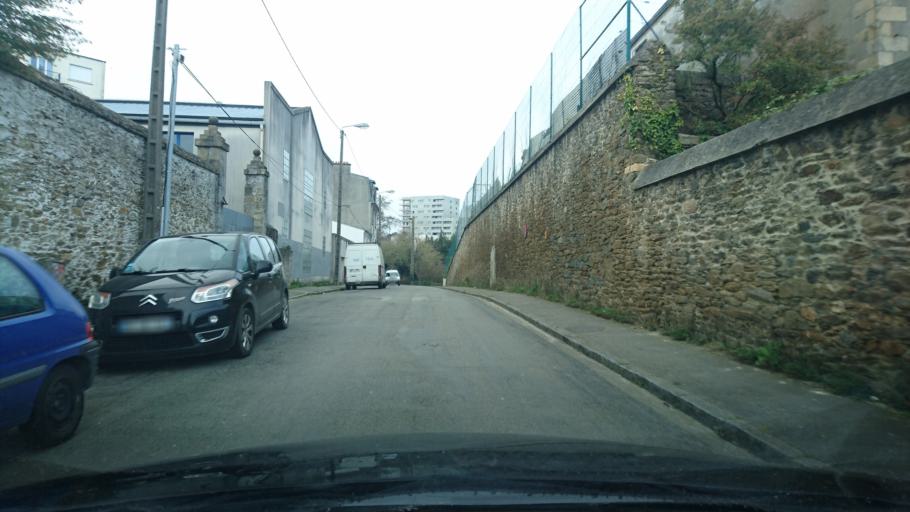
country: FR
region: Brittany
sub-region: Departement du Finistere
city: Brest
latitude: 48.3880
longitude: -4.5004
